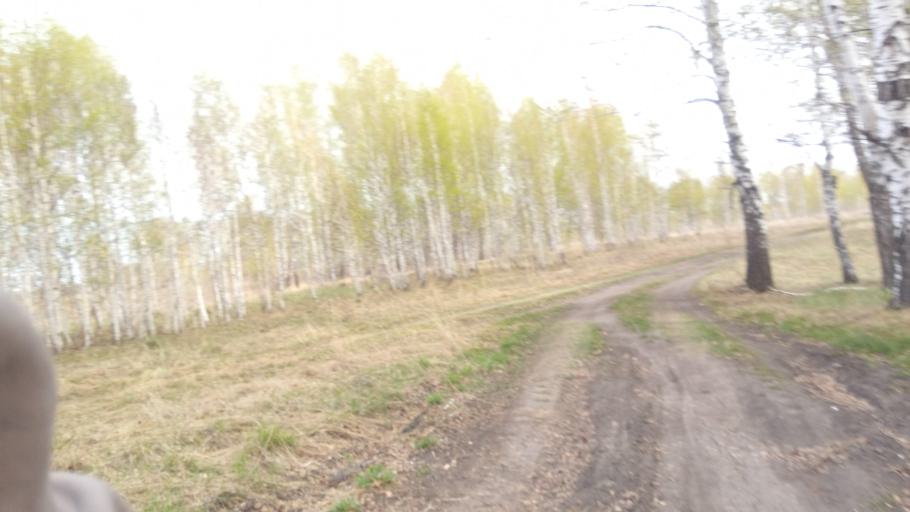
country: RU
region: Chelyabinsk
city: Timiryazevskiy
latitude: 55.0058
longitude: 60.8596
